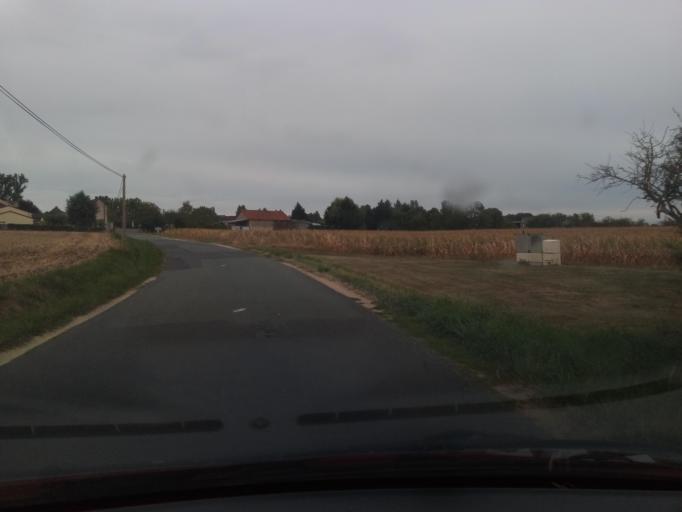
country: FR
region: Poitou-Charentes
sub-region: Departement de la Vienne
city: Saint-Savin
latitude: 46.5098
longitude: 0.7747
